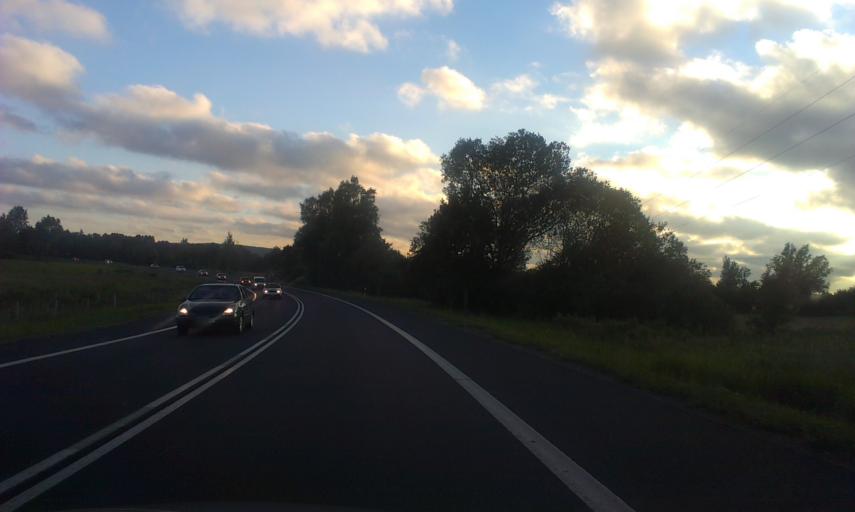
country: PL
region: West Pomeranian Voivodeship
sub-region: Powiat slawienski
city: Darlowo
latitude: 54.2971
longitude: 16.4994
